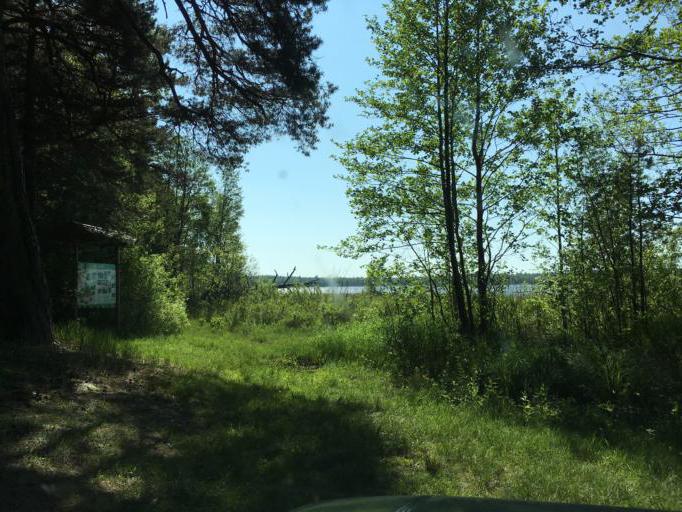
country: LV
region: Ventspils
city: Ventspils
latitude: 57.4703
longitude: 21.7720
